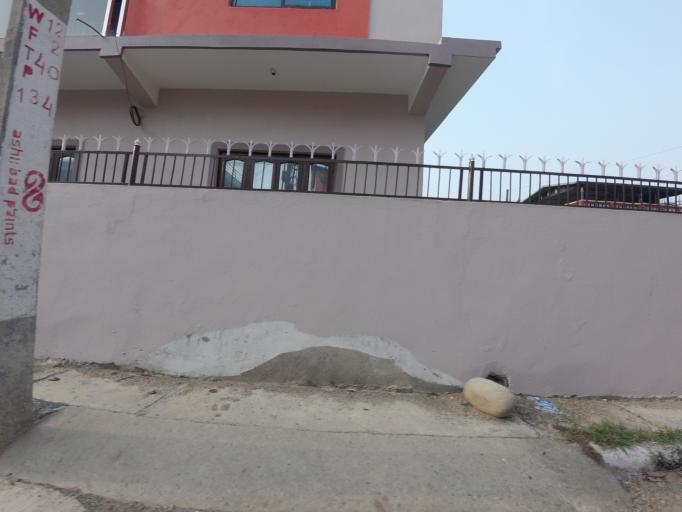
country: NP
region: Western Region
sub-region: Lumbini Zone
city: Bhairahawa
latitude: 27.5114
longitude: 83.4559
